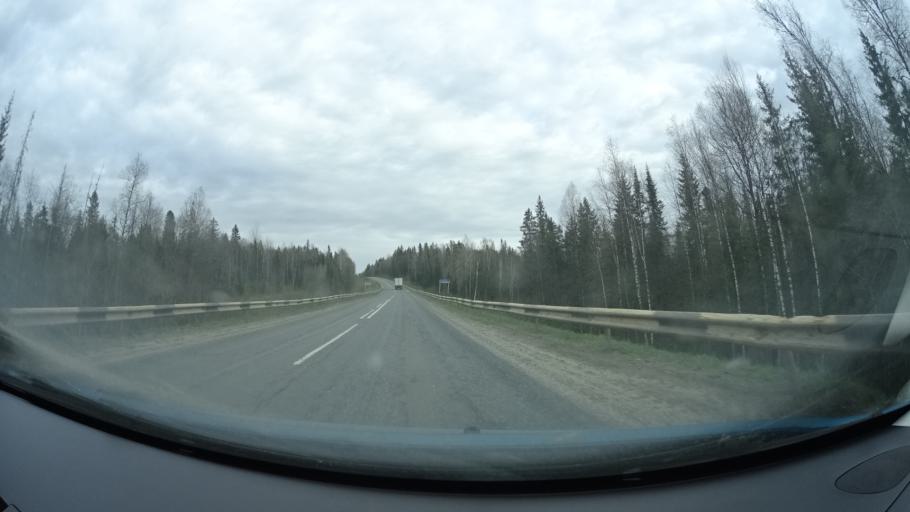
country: RU
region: Perm
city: Yugo-Kamskiy
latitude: 57.6150
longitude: 55.6295
